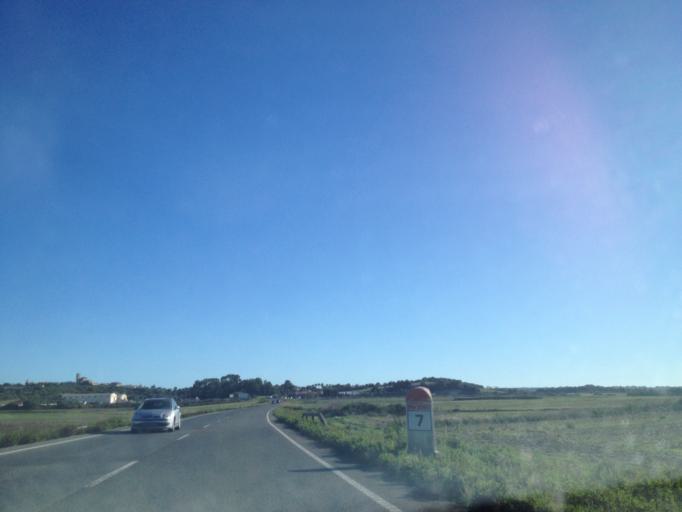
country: ES
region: Balearic Islands
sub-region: Illes Balears
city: Ariany
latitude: 39.6459
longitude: 3.0918
